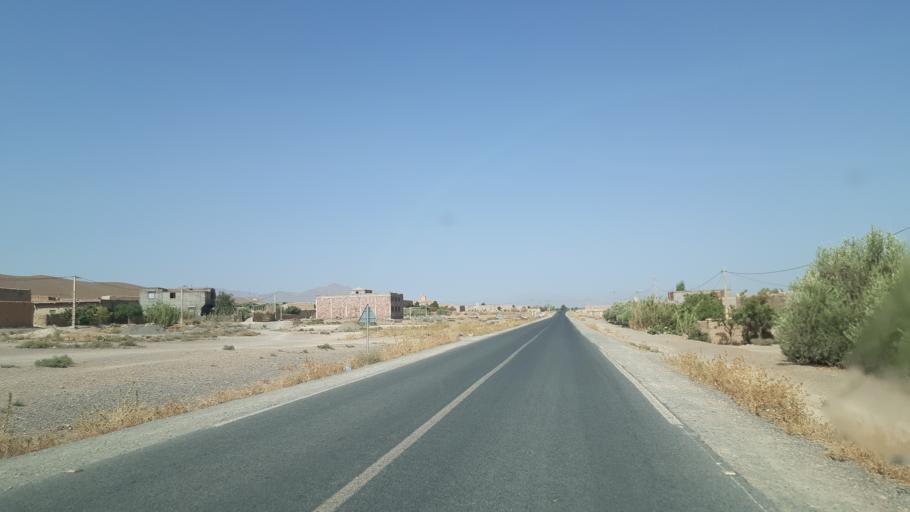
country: MA
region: Meknes-Tafilalet
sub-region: Errachidia
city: Errachidia
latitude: 32.2528
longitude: -4.5705
